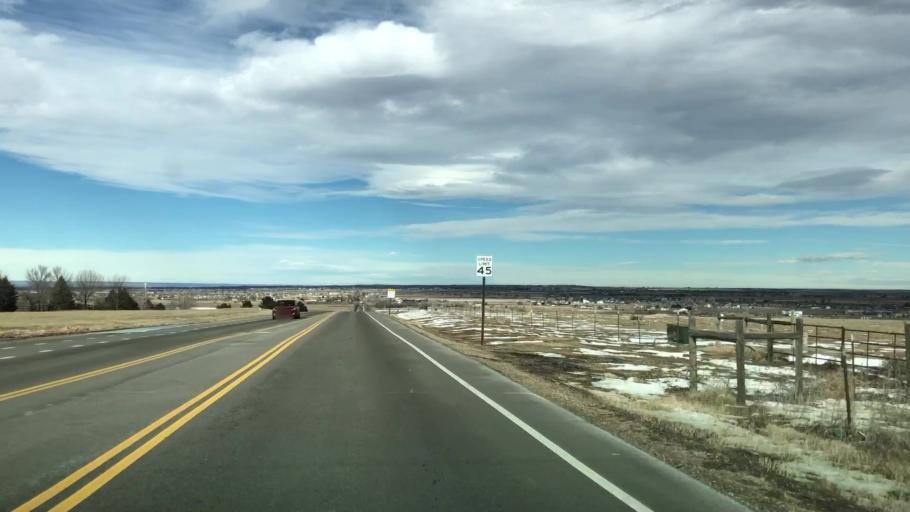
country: US
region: Colorado
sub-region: Weld County
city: Windsor
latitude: 40.4647
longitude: -104.9441
